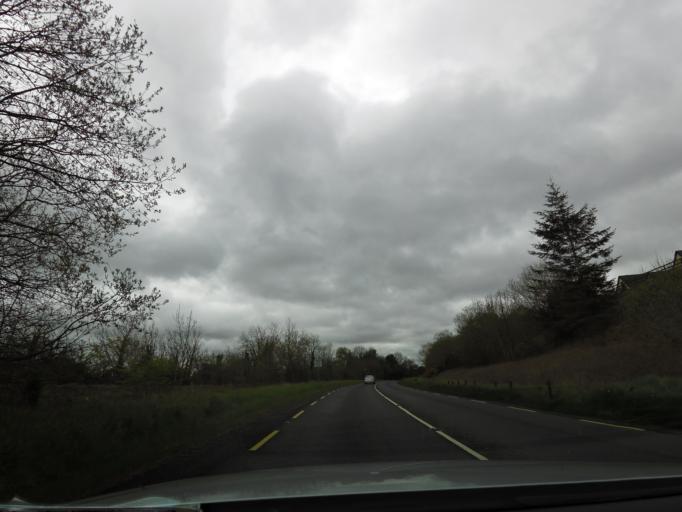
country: IE
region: Leinster
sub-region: Kilkenny
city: Kilkenny
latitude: 52.6917
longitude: -7.2788
